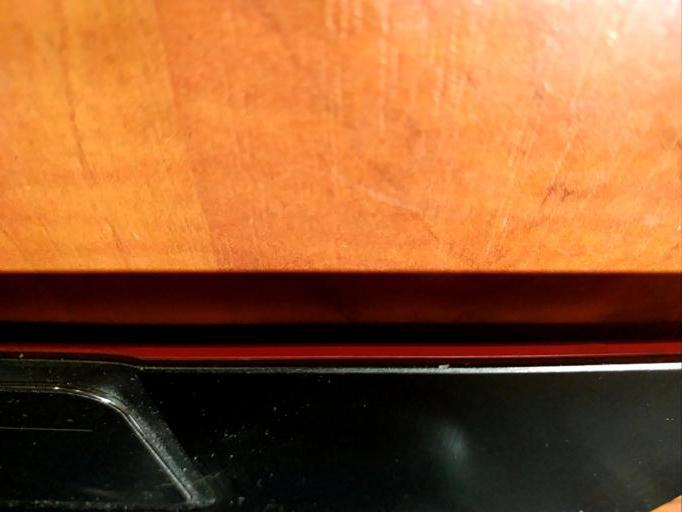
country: RU
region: Tverskaya
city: Ves'yegonsk
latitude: 58.7447
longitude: 37.5438
